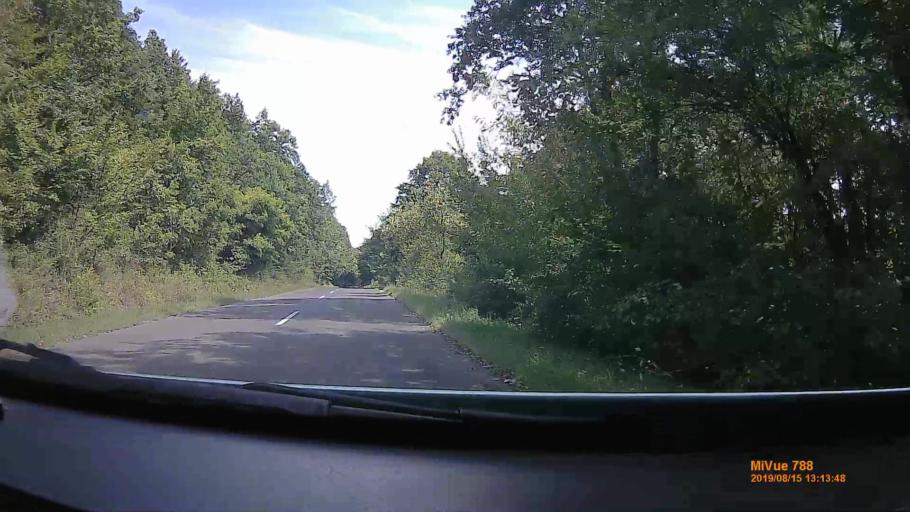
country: HU
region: Borsod-Abauj-Zemplen
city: Sajobabony
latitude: 48.1475
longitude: 20.6743
